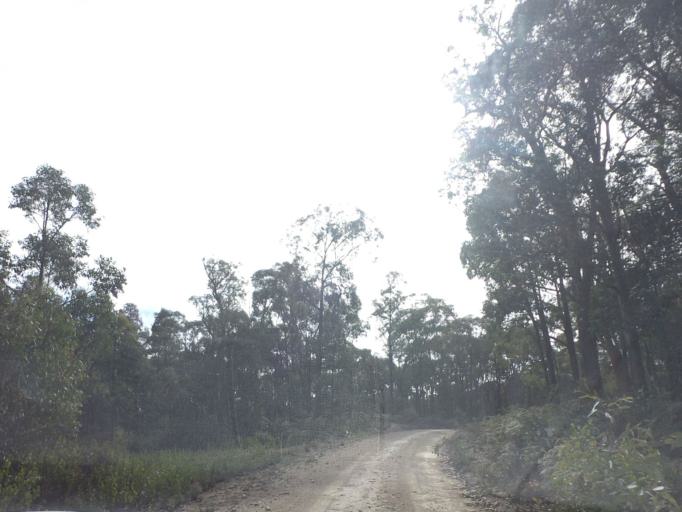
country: AU
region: Victoria
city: Brown Hill
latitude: -37.4918
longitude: 144.1841
